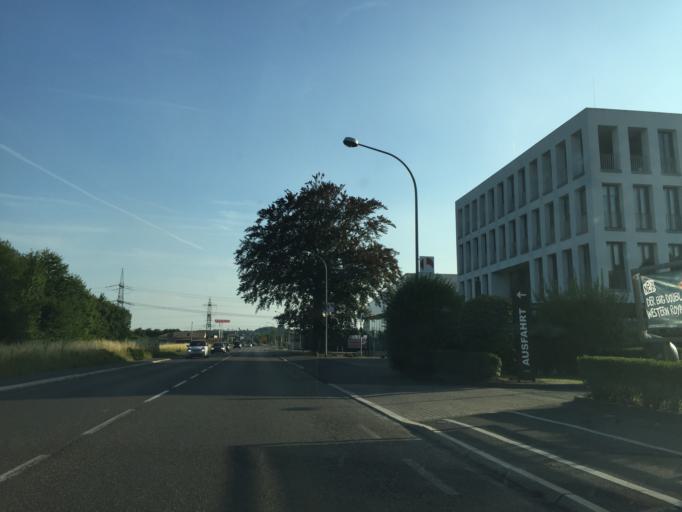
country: DE
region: North Rhine-Westphalia
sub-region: Regierungsbezirk Koln
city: Hurth
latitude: 50.8915
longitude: 6.9021
